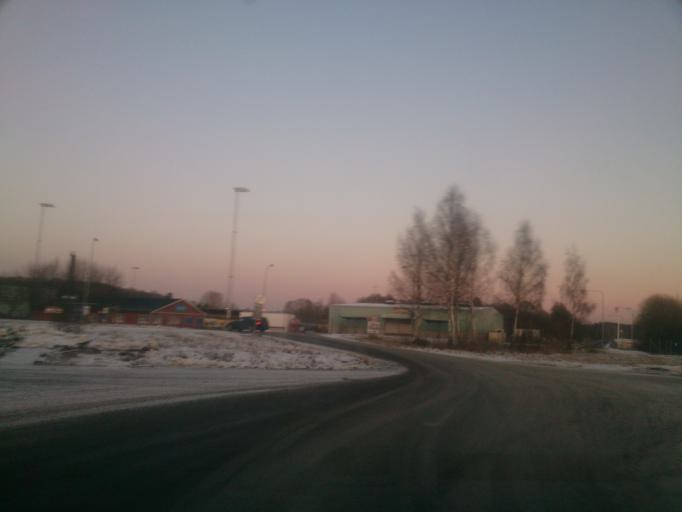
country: SE
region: OEstergoetland
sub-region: Norrkopings Kommun
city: Norrkoping
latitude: 58.6101
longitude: 16.1674
